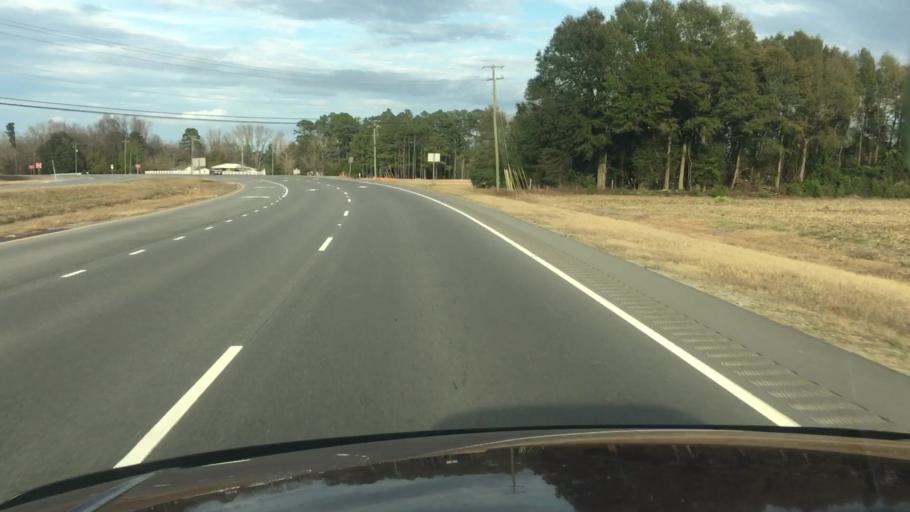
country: US
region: North Carolina
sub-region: Cumberland County
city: Hope Mills
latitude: 34.9351
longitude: -78.8483
